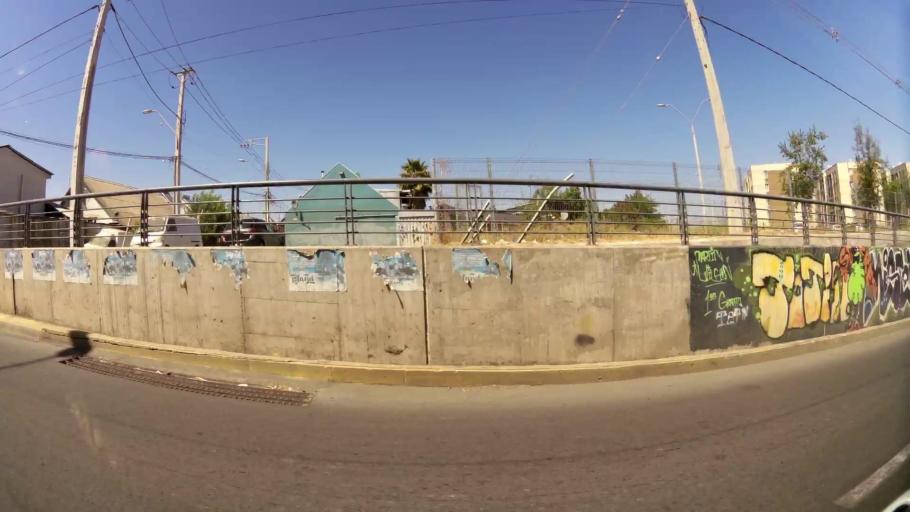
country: CL
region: Maule
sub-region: Provincia de Curico
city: Curico
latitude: -34.9700
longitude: -71.2384
